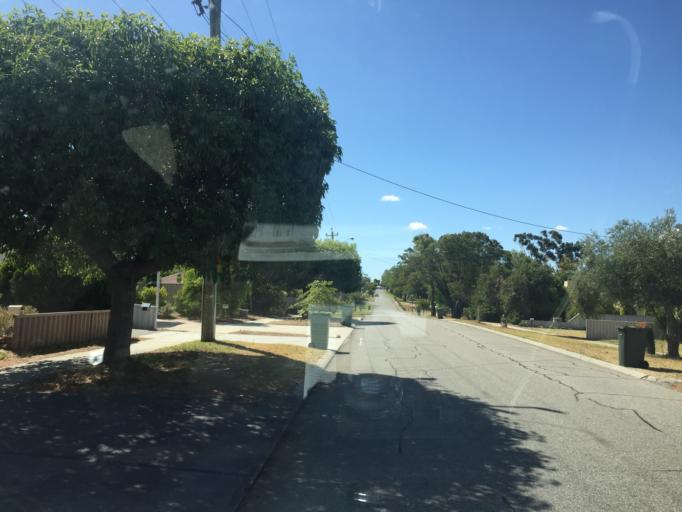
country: AU
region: Western Australia
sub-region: Belmont
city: Redcliffe
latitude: -31.9372
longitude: 115.9424
